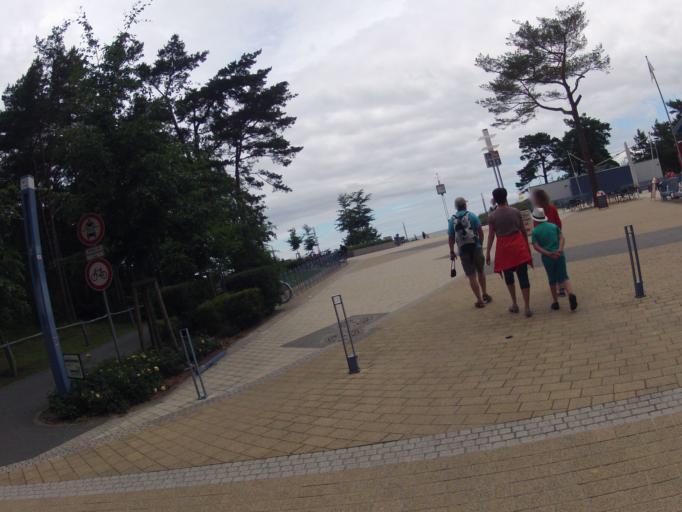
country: DE
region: Mecklenburg-Vorpommern
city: Ostseebad Zinnowitz
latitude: 54.0705
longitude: 13.9535
